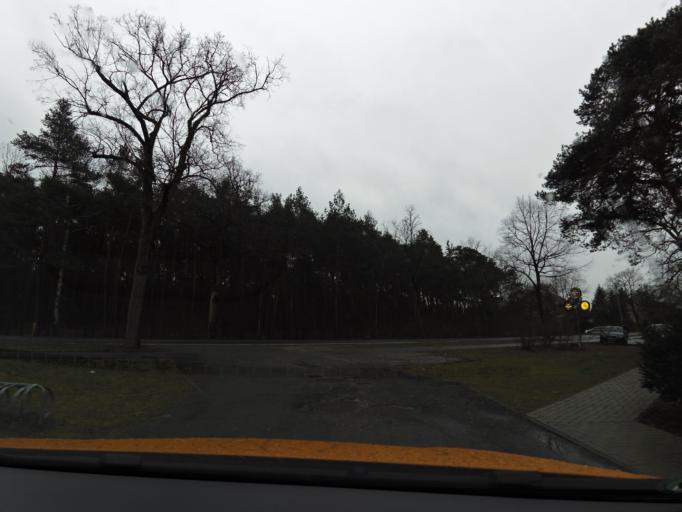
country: DE
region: Brandenburg
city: Am Mellensee
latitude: 52.1906
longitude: 13.4235
